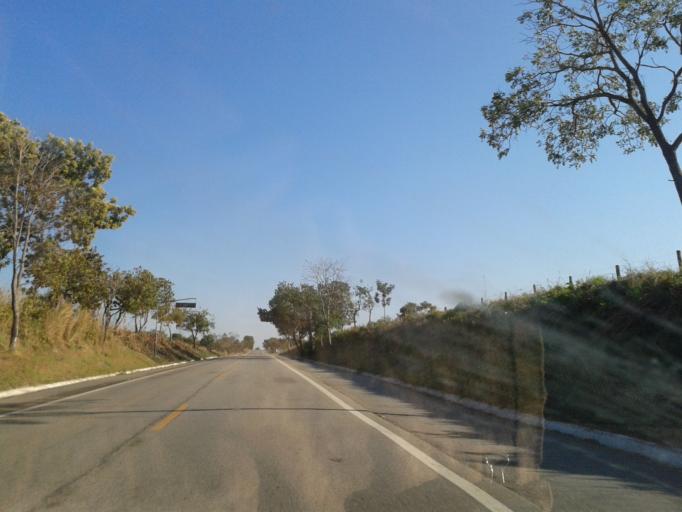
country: BR
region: Goias
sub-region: Mozarlandia
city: Mozarlandia
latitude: -15.2647
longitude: -50.4887
